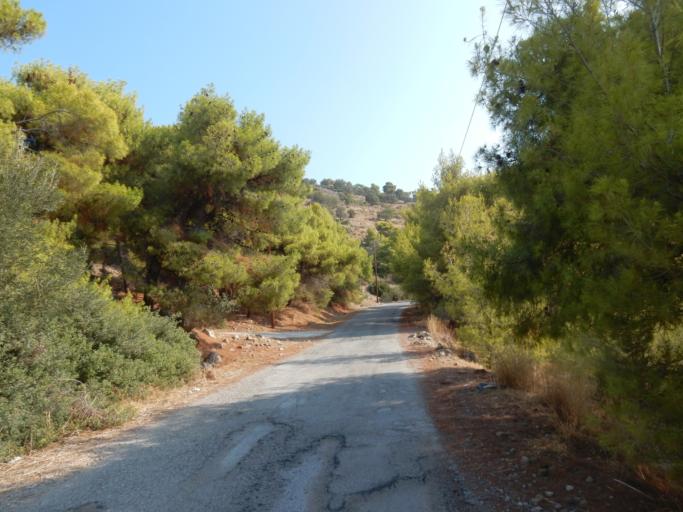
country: GR
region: Attica
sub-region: Nomos Piraios
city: Vathi
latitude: 37.7246
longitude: 23.5233
